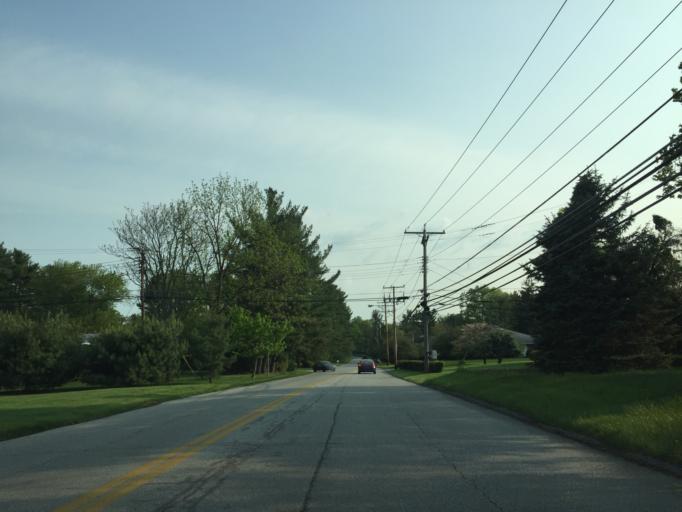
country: US
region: Maryland
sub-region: Baltimore County
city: Pikesville
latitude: 39.3934
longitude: -76.7125
